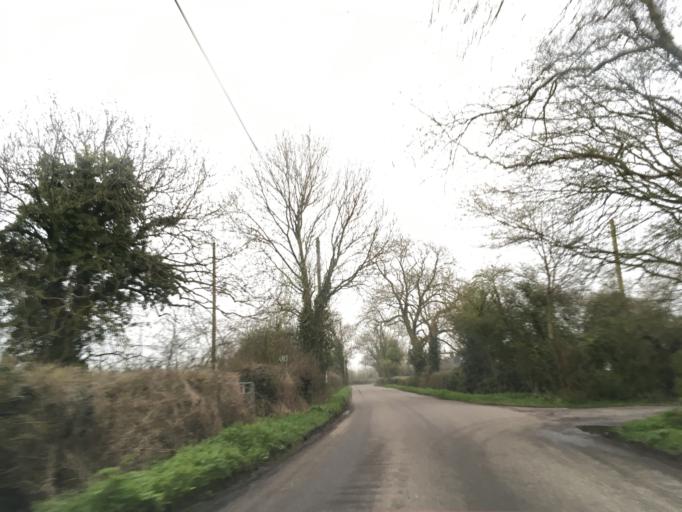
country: GB
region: England
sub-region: South Gloucestershire
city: Alveston
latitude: 51.5558
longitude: -2.5277
